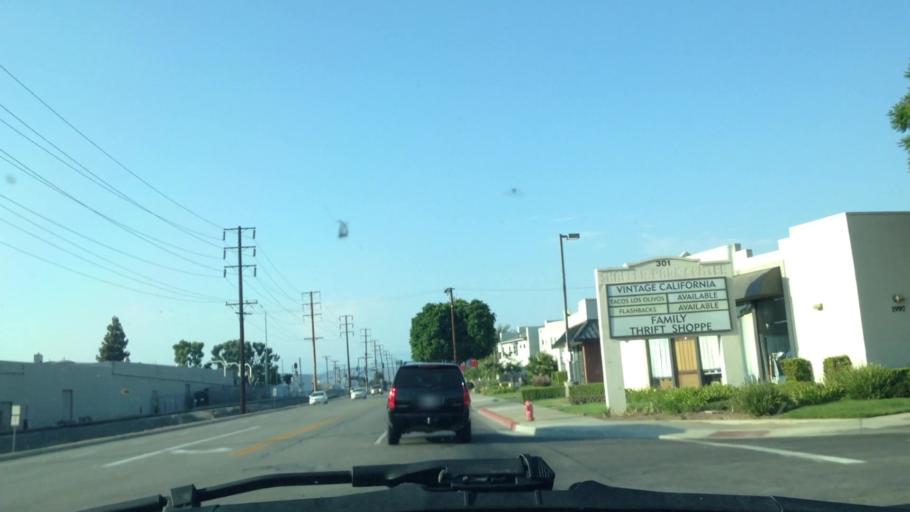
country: US
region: California
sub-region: Orange County
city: Orange
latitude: 33.8207
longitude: -117.8514
